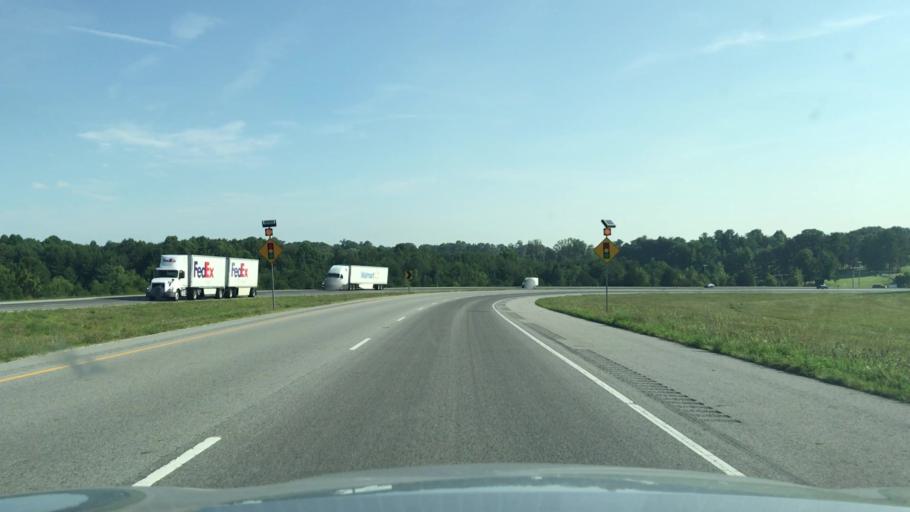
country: US
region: Tennessee
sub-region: Putnam County
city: Algood
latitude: 36.2008
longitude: -85.4604
